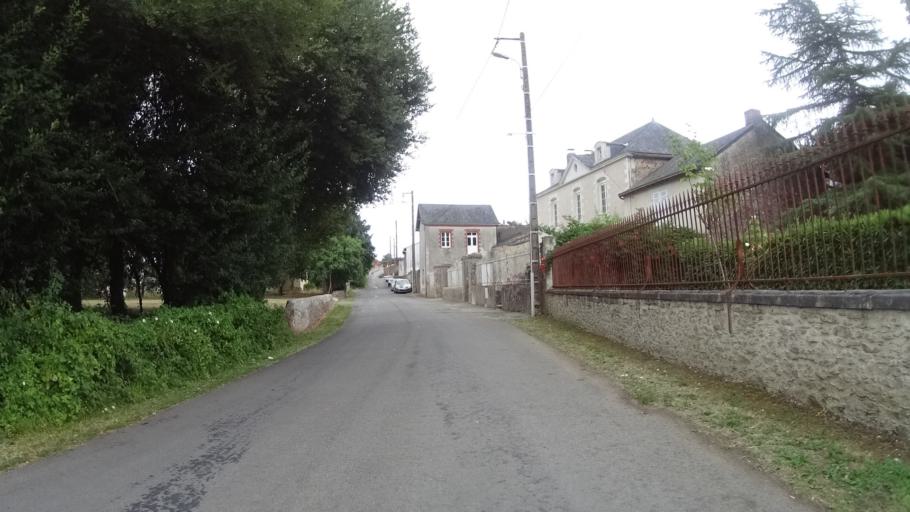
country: FR
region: Pays de la Loire
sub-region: Departement de la Loire-Atlantique
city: Le Pellerin
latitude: 47.2059
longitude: -1.7816
